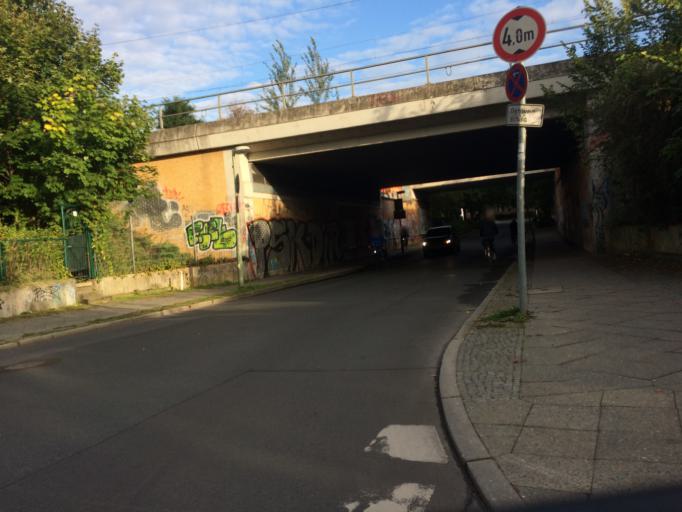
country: DE
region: Berlin
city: Pankow
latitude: 52.5622
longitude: 13.4029
